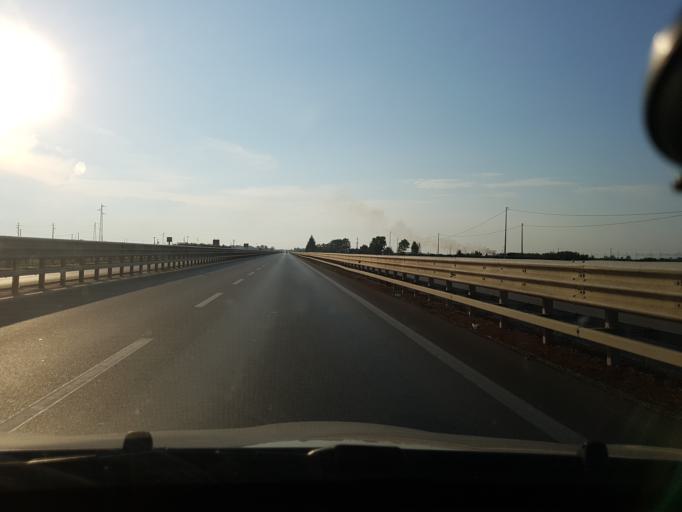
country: IT
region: Apulia
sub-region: Provincia di Foggia
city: Orta Nova
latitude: 41.3507
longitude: 15.7273
